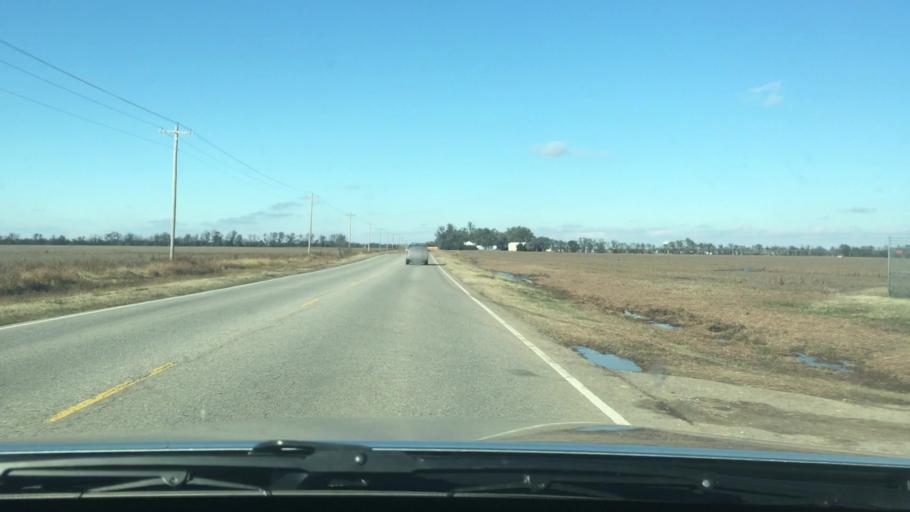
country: US
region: Kansas
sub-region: Sedgwick County
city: Maize
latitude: 37.7446
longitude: -97.4809
